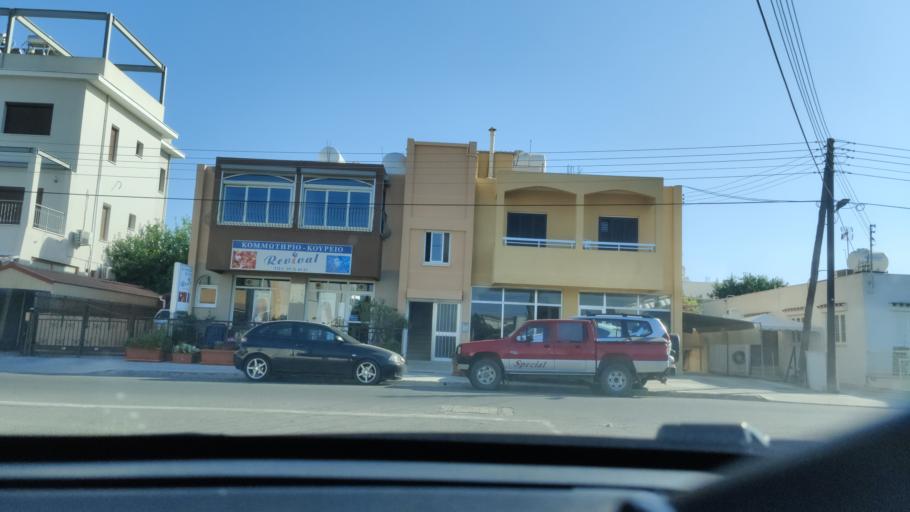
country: CY
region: Lefkosia
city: Tseri
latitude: 35.1193
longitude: 33.3246
